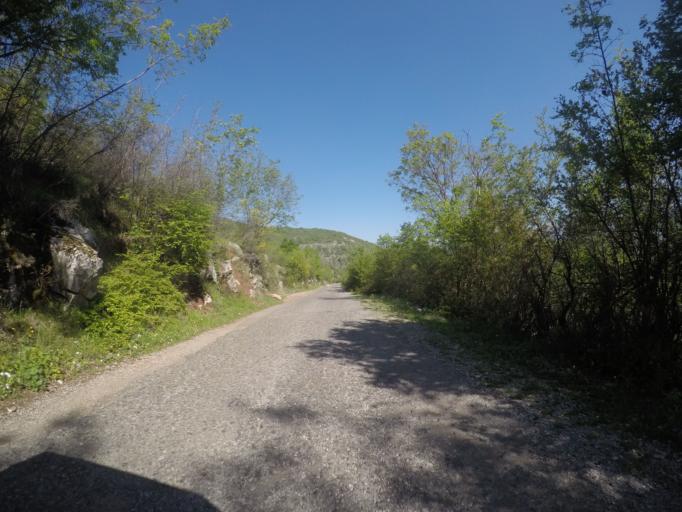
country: ME
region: Danilovgrad
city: Danilovgrad
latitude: 42.5300
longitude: 19.0916
